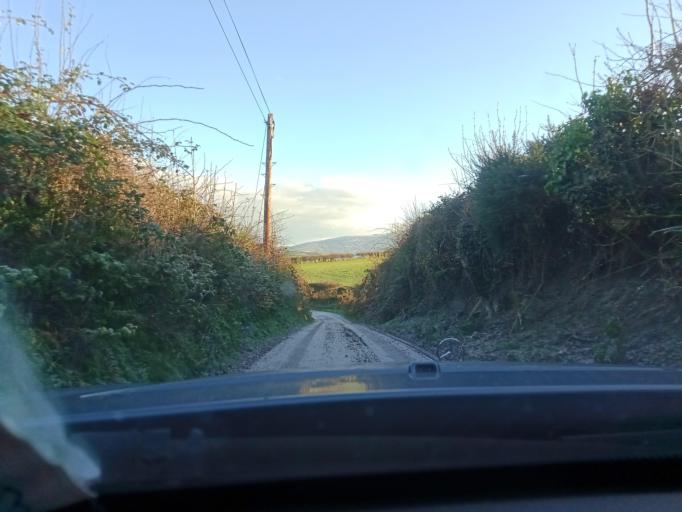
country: IE
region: Leinster
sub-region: Kilkenny
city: Graiguenamanagh
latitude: 52.5651
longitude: -6.9354
